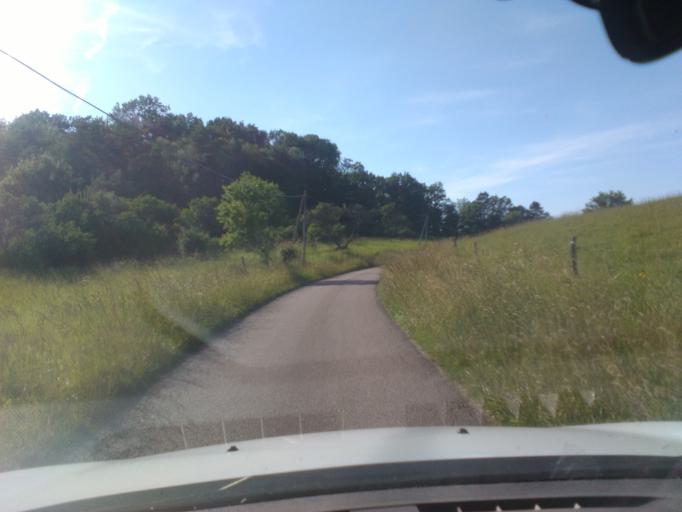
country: FR
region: Lorraine
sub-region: Departement des Vosges
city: Mirecourt
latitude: 48.2529
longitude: 6.2281
